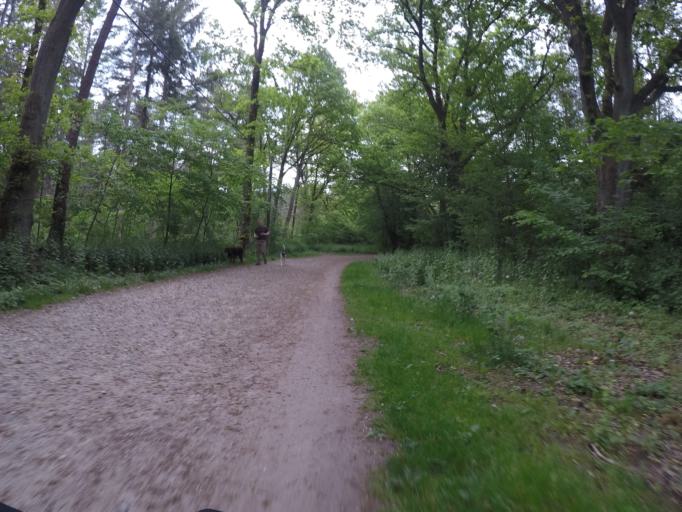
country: DE
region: Schleswig-Holstein
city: Norderstedt
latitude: 53.7140
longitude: 9.9786
